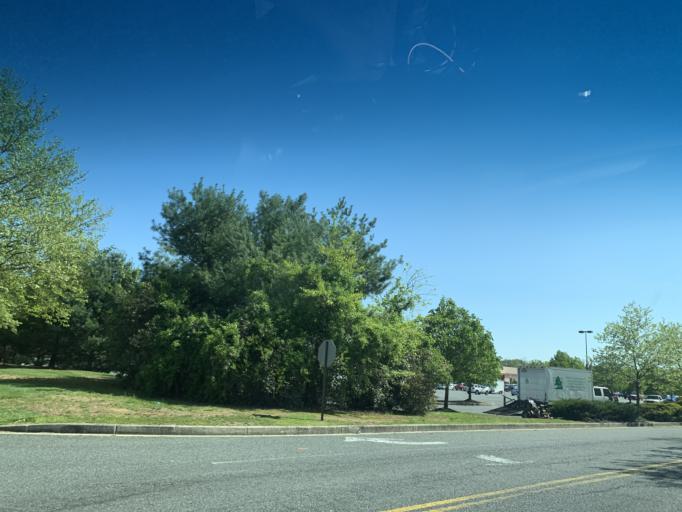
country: US
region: Maryland
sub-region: Harford County
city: Edgewood
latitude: 39.4410
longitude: -76.2919
